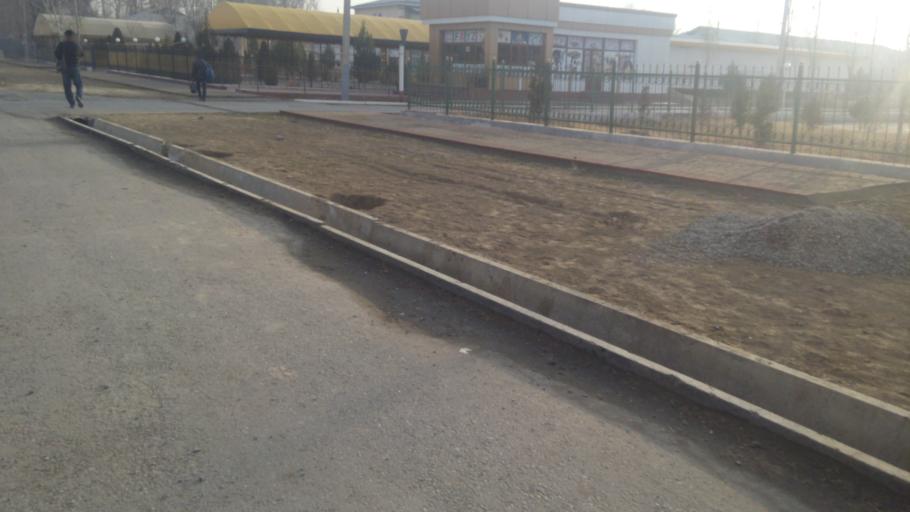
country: UZ
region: Sirdaryo
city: Guliston
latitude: 40.5121
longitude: 68.7796
